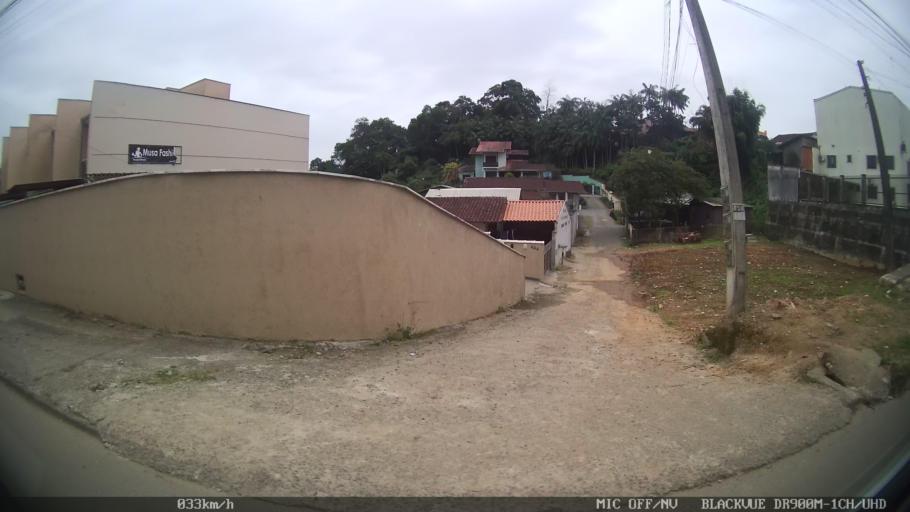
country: BR
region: Santa Catarina
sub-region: Joinville
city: Joinville
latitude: -26.3491
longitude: -48.8238
